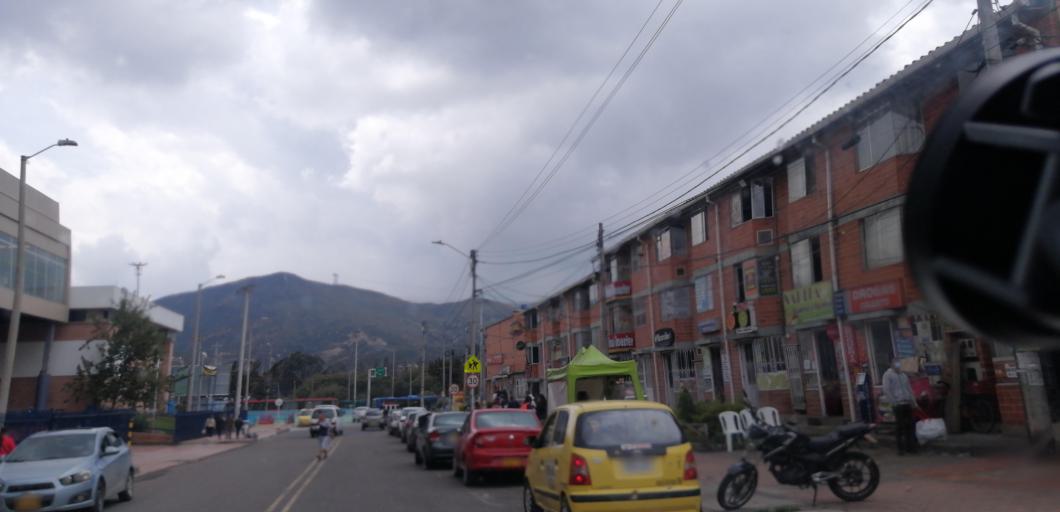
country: CO
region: Bogota D.C.
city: Bogota
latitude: 4.5333
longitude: -74.1182
